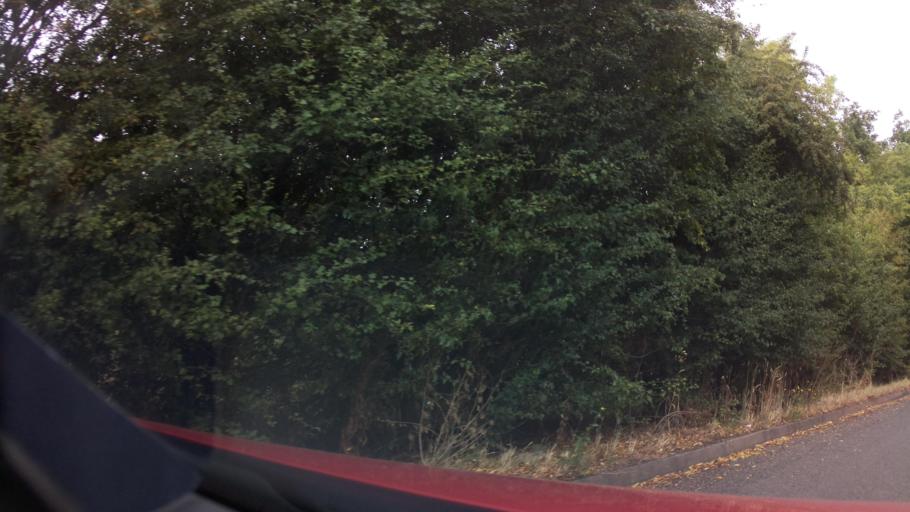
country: GB
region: England
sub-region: Derbyshire
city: Long Eaton
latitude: 52.9235
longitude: -1.3103
